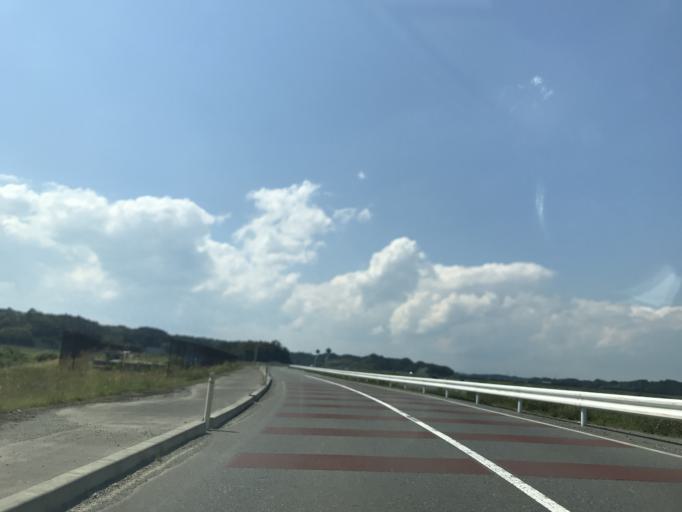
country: JP
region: Miyagi
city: Yamoto
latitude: 38.3888
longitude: 141.1613
